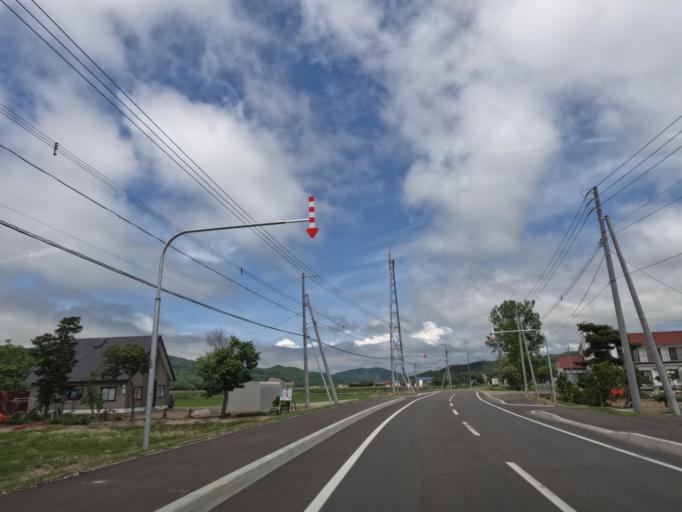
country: JP
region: Hokkaido
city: Tobetsu
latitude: 43.2716
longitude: 141.5304
